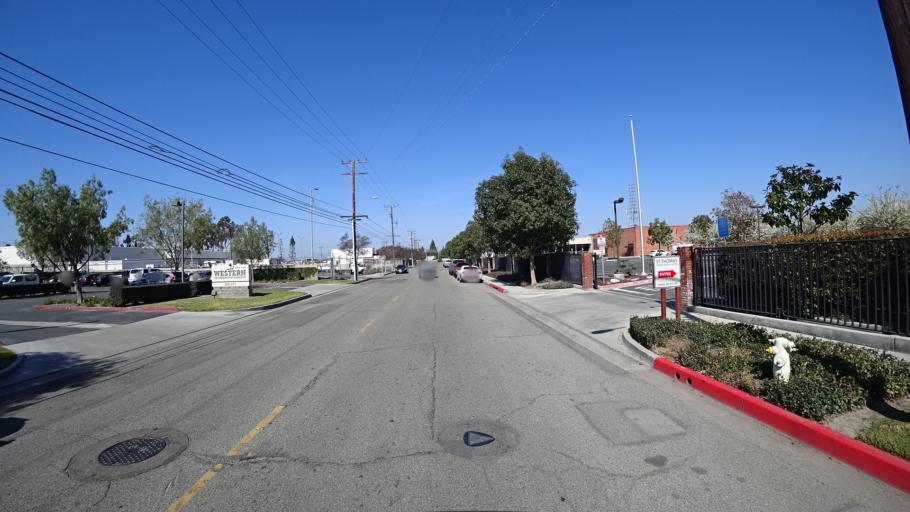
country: US
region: California
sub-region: Orange County
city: Anaheim
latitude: 33.8362
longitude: -117.9473
